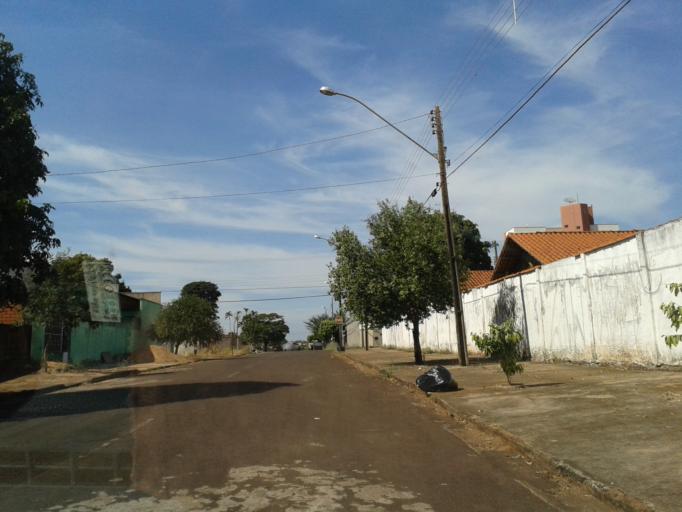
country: BR
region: Minas Gerais
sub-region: Ituiutaba
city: Ituiutaba
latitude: -18.9621
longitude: -49.4677
